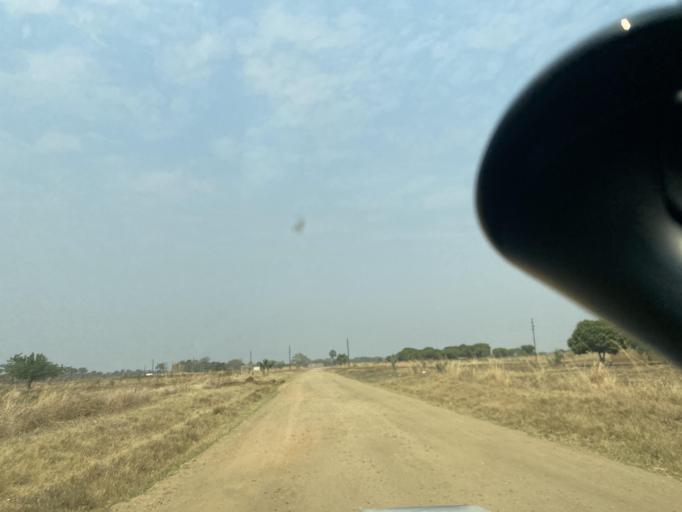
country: ZM
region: Lusaka
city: Kafue
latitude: -15.6512
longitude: 28.0566
